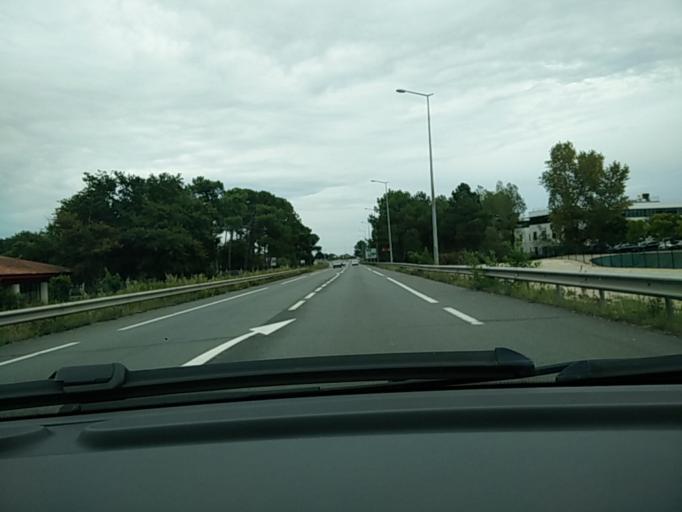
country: FR
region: Aquitaine
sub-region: Departement de la Gironde
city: Le Haillan
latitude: 44.8331
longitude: -0.6849
